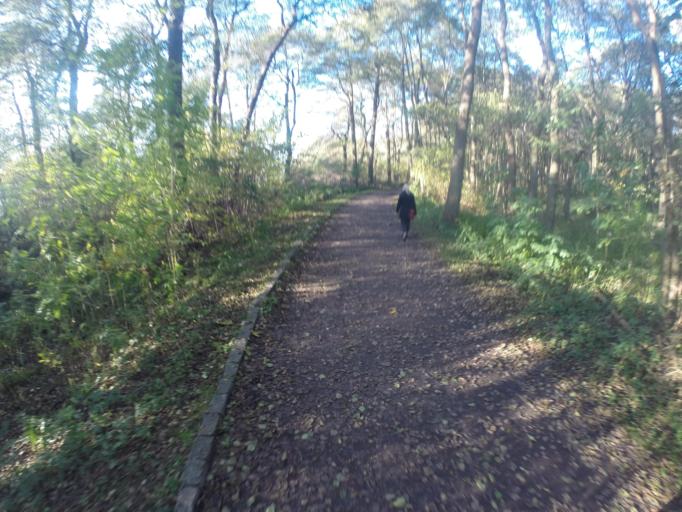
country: DK
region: Capital Region
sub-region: Gladsaxe Municipality
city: Buddinge
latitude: 55.7693
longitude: 12.4695
